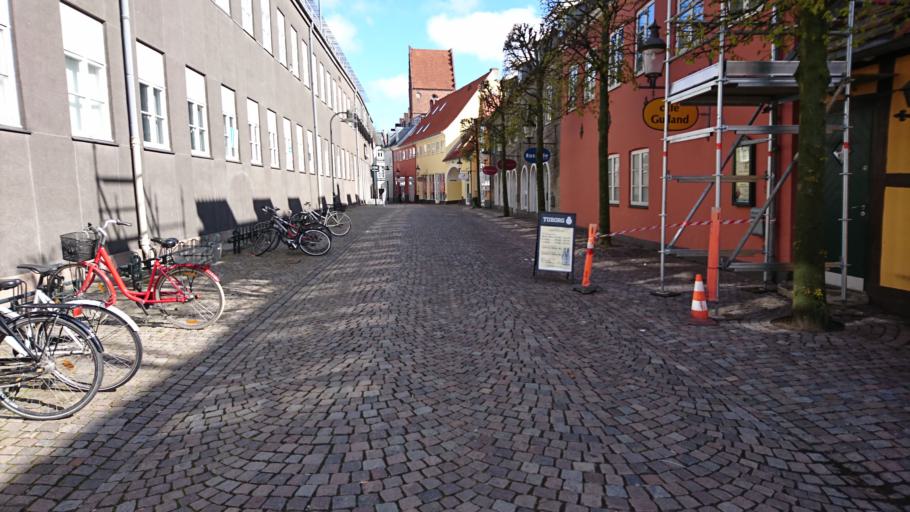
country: DK
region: Zealand
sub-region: Roskilde Kommune
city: Roskilde
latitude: 55.6401
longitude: 12.0799
